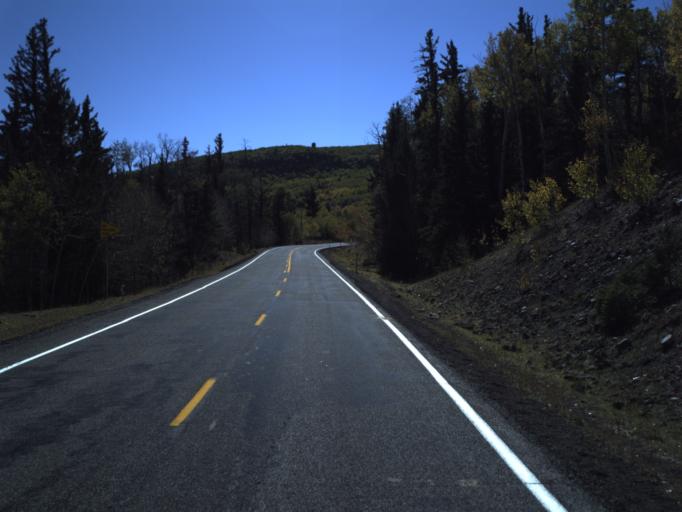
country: US
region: Utah
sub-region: Wayne County
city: Loa
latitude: 38.0772
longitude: -111.3391
